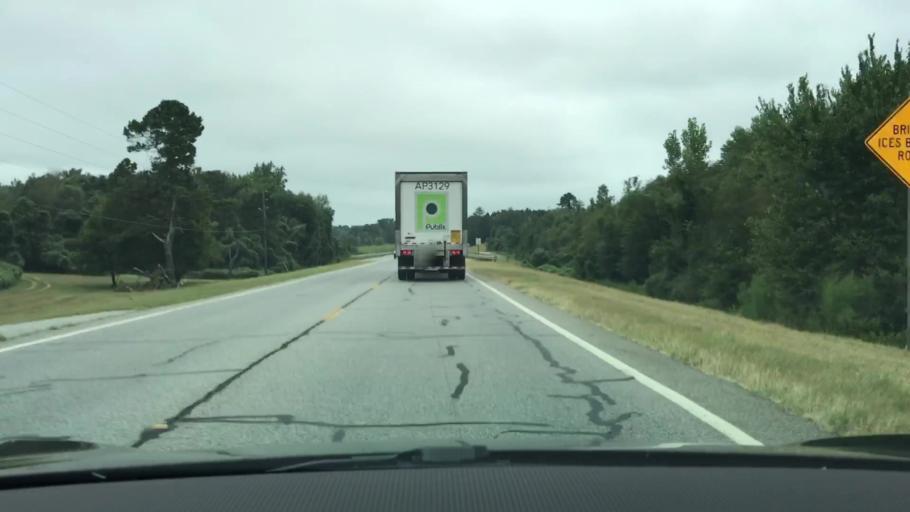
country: US
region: Georgia
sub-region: Oconee County
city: Watkinsville
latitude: 33.7331
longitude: -83.3030
